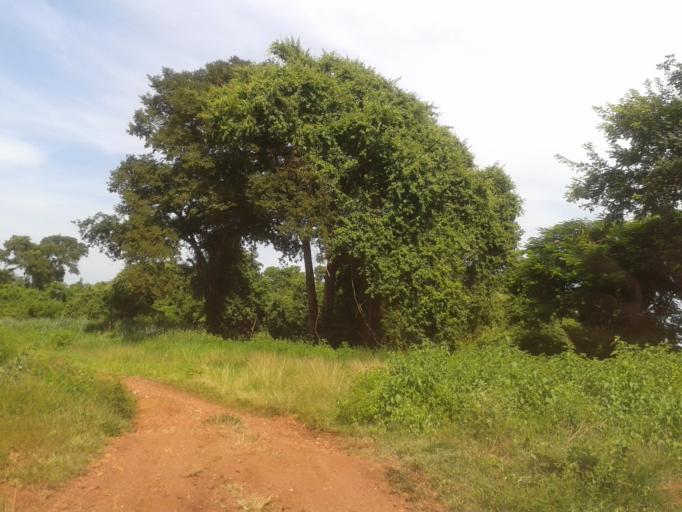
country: BR
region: Minas Gerais
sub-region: Santa Vitoria
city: Santa Vitoria
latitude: -19.1308
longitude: -50.5507
